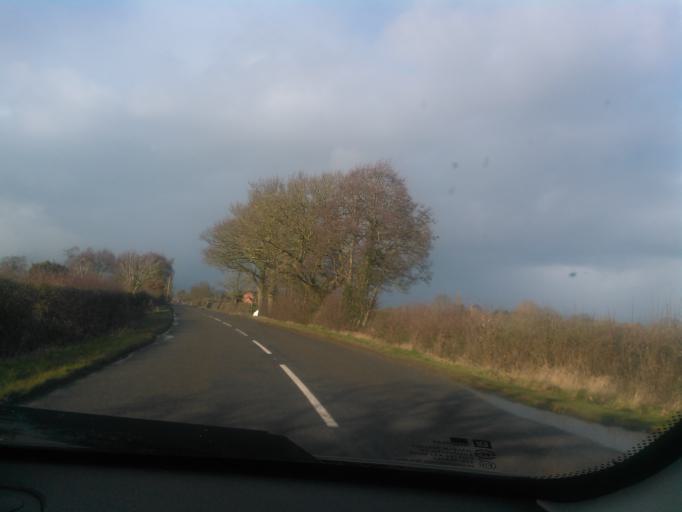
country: GB
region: England
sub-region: Shropshire
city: Shawbury
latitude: 52.7758
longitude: -2.6375
